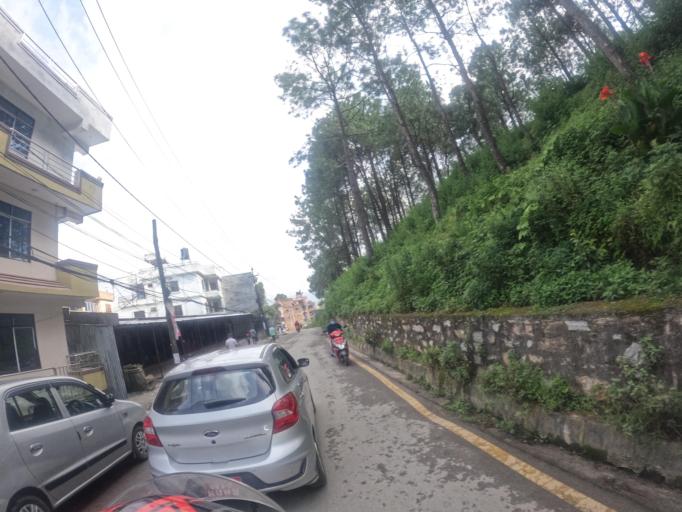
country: NP
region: Central Region
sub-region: Bagmati Zone
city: Bhaktapur
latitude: 27.6662
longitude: 85.3862
